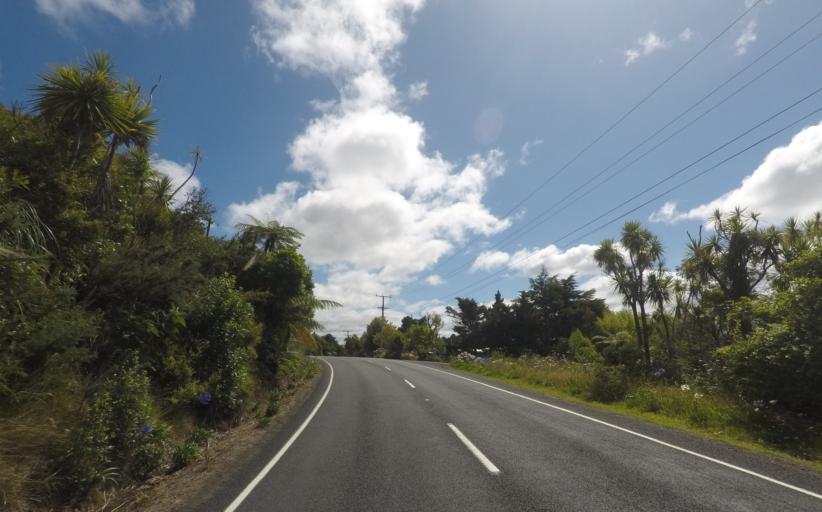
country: NZ
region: Auckland
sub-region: Auckland
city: Muriwai Beach
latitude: -36.8591
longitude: 174.5219
